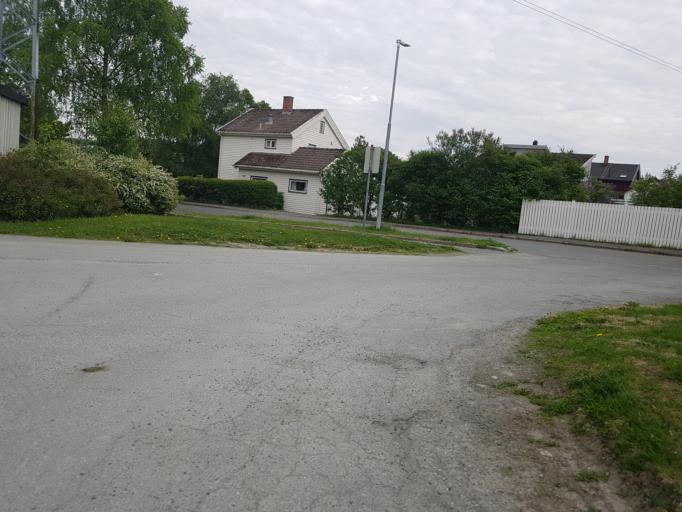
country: NO
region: Sor-Trondelag
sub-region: Trondheim
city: Trondheim
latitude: 63.4251
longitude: 10.4501
